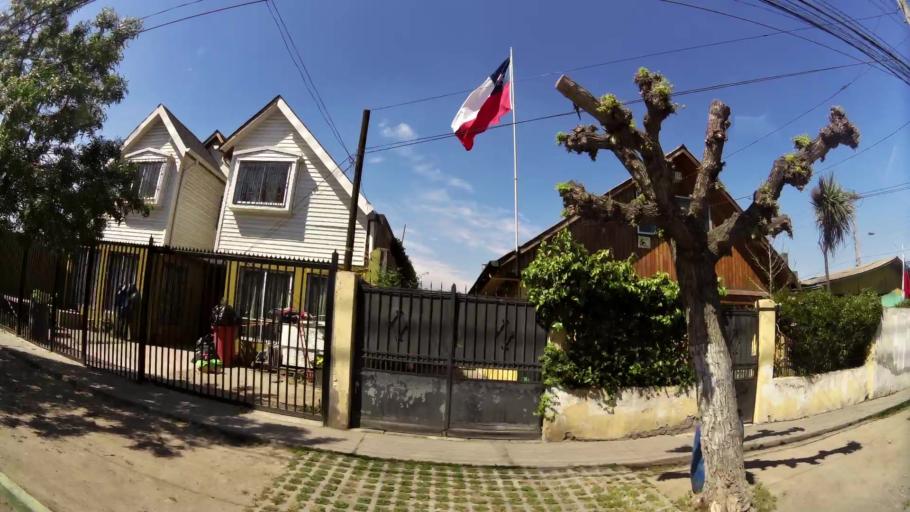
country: CL
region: Santiago Metropolitan
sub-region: Provincia de Santiago
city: La Pintana
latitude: -33.5269
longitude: -70.6385
